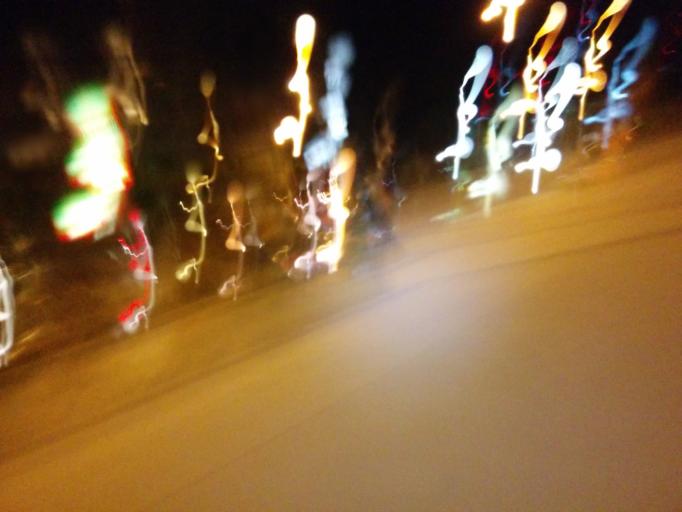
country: US
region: Washington
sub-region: King County
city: Seattle
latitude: 47.6271
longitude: -122.3394
